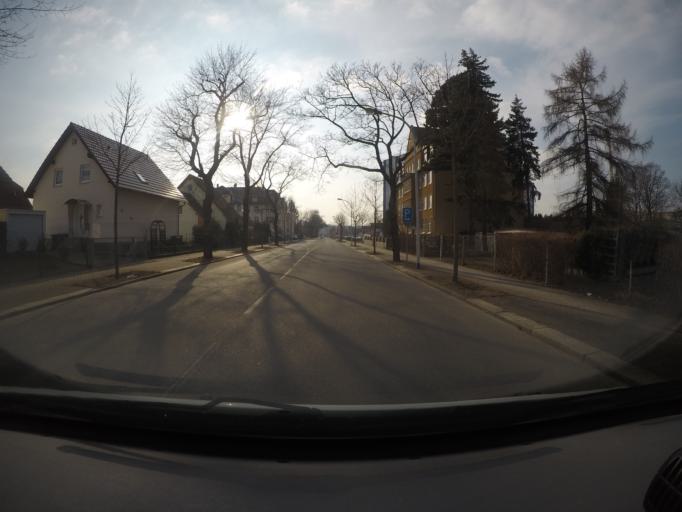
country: DE
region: Saxony
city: Chemnitz
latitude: 50.7958
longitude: 12.9259
